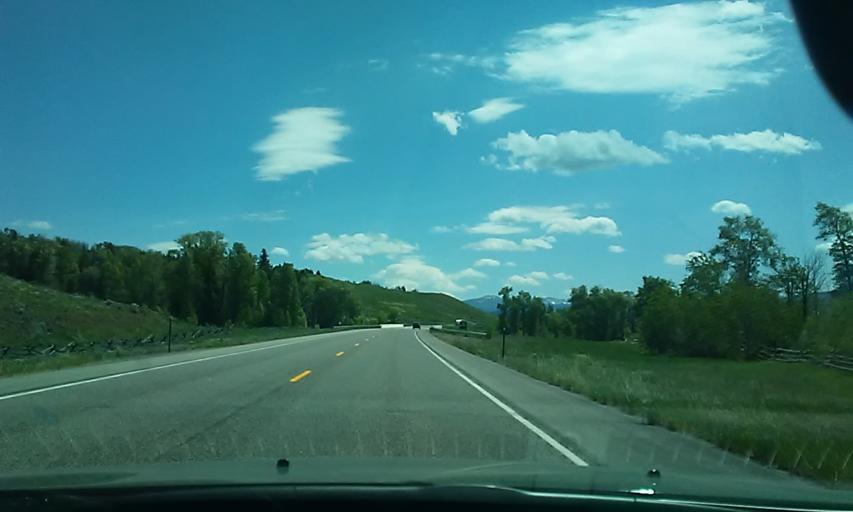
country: US
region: Wyoming
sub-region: Teton County
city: Jackson
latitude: 43.8401
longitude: -110.4601
